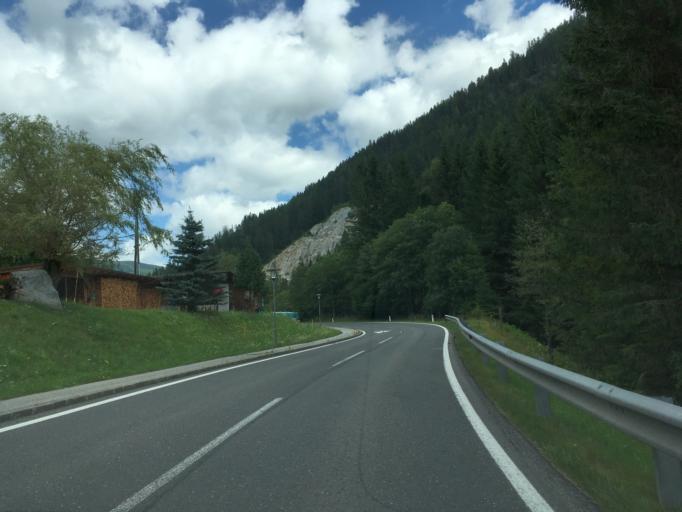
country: AT
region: Carinthia
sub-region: Politischer Bezirk Spittal an der Drau
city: Kleinkirchheim
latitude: 46.8261
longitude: 13.7700
